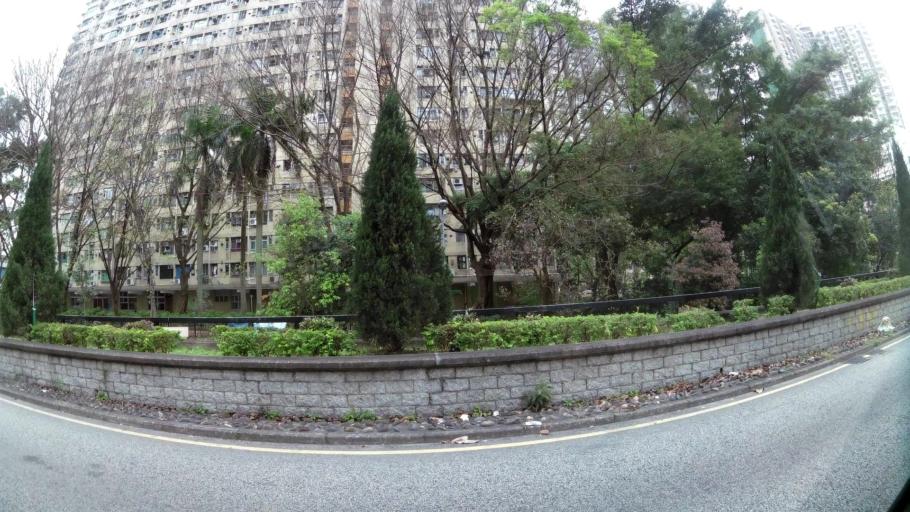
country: HK
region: Tai Po
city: Tai Po
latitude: 22.4525
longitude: 114.1626
